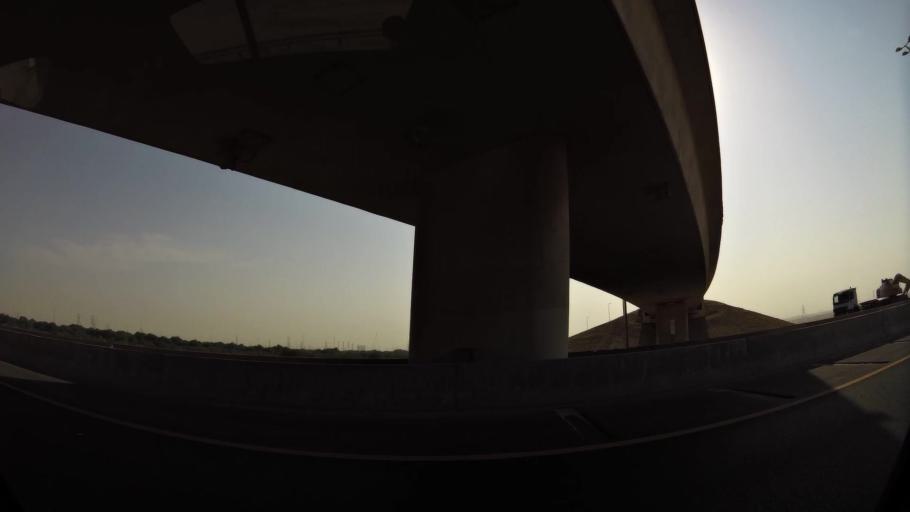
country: KW
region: Al Ahmadi
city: Al Ahmadi
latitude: 29.0473
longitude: 48.0949
